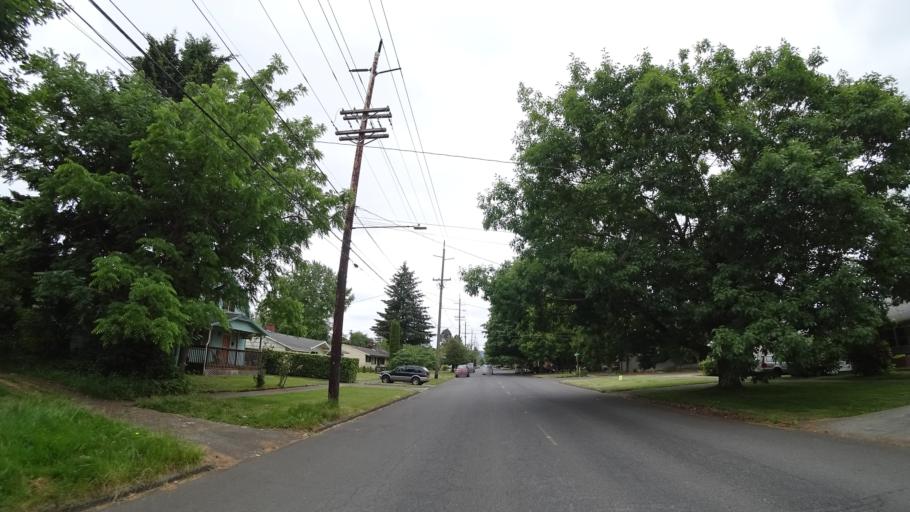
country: US
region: Oregon
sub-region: Multnomah County
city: Portland
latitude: 45.5840
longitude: -122.7038
